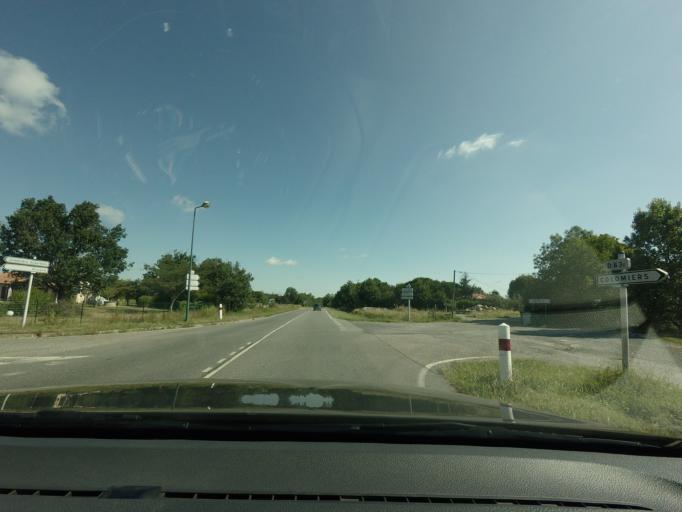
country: FR
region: Midi-Pyrenees
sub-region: Departement de la Haute-Garonne
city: Cornebarrieu
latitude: 43.6417
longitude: 1.3335
